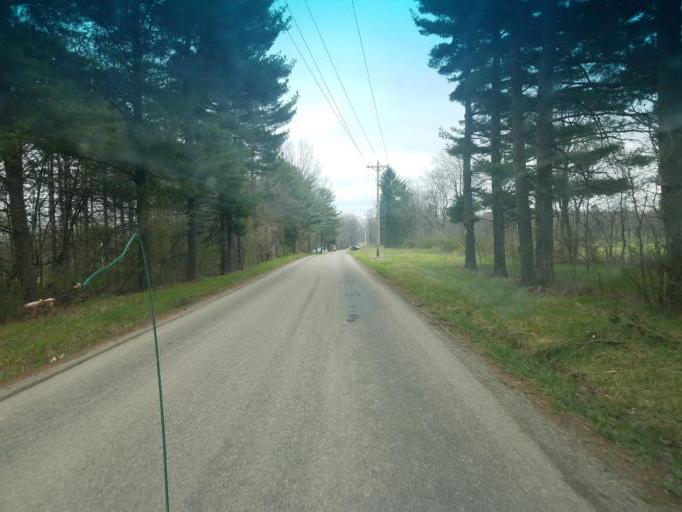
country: US
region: Ohio
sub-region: Stark County
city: Beach City
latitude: 40.6299
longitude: -81.6521
